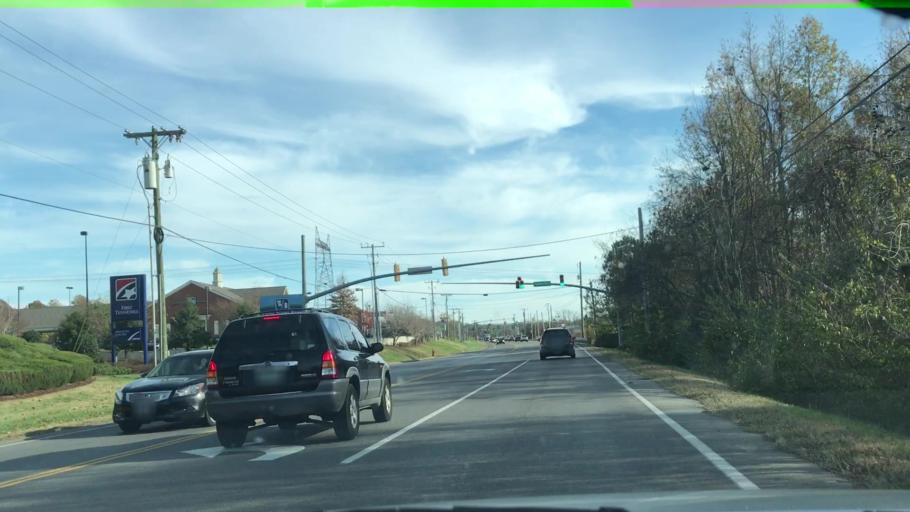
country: US
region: Tennessee
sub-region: Williamson County
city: Nolensville
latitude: 35.9998
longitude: -86.6940
